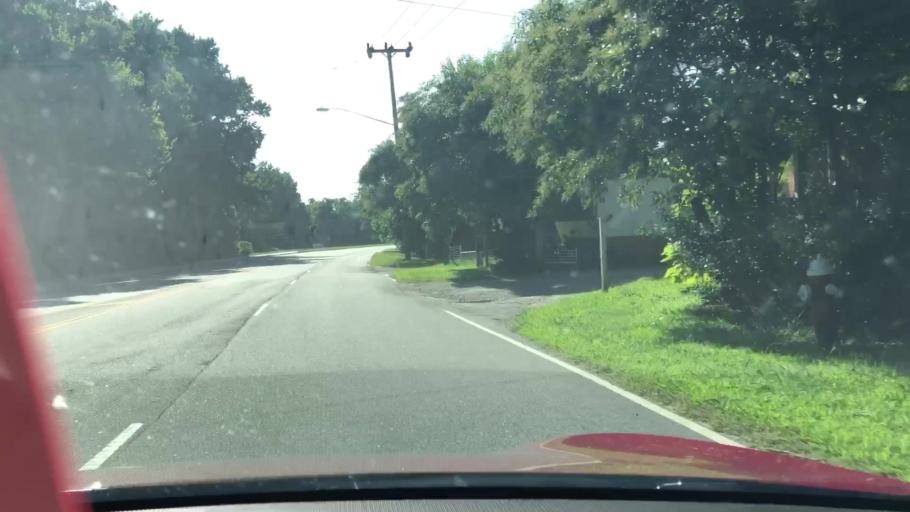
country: US
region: Virginia
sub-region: City of Virginia Beach
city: Virginia Beach
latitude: 36.8419
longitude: -75.9981
